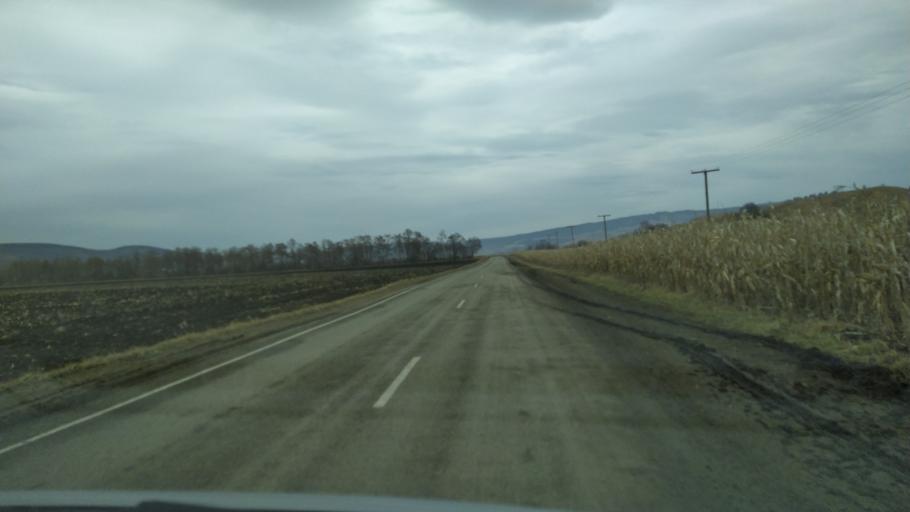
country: RU
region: Krasnodarskiy
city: Peredovaya
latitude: 44.1066
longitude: 41.4241
